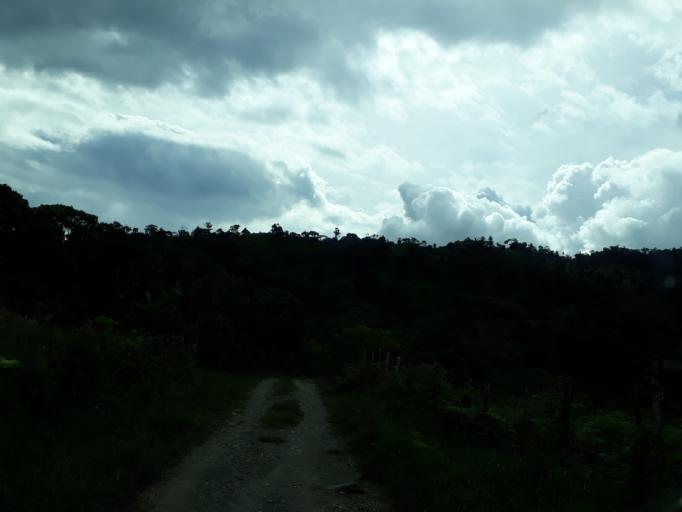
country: CO
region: Boyaca
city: Muzo
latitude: 5.3871
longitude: -74.1035
